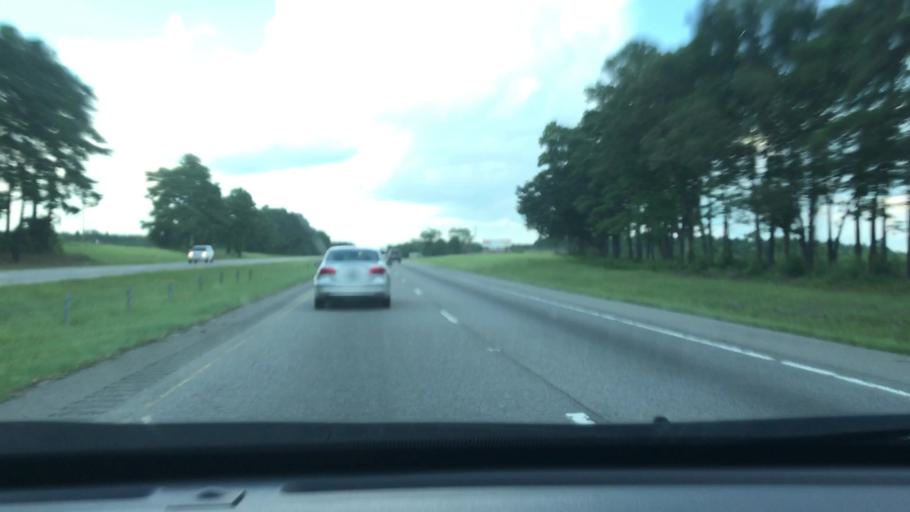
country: US
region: North Carolina
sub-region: Robeson County
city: Saint Pauls
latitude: 34.8626
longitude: -78.9649
